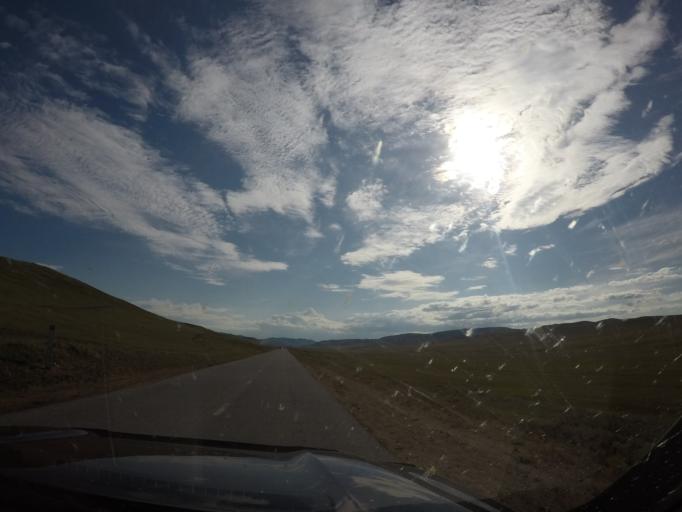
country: MN
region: Hentiy
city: Modot
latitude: 47.7532
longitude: 108.6234
